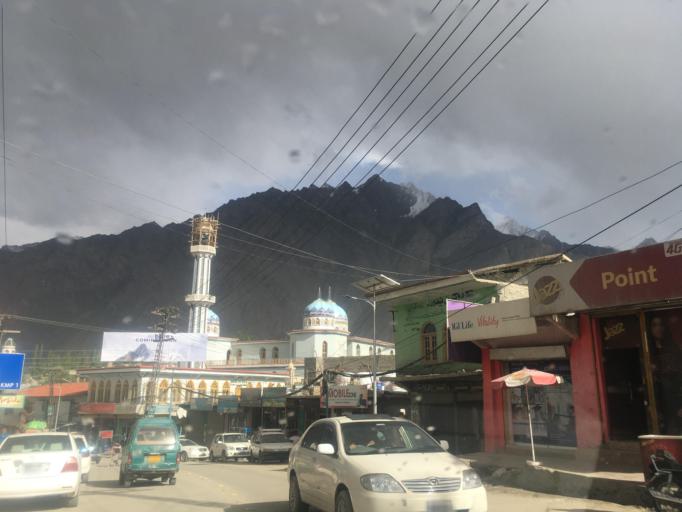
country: PK
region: Gilgit-Baltistan
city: Skardu
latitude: 35.2979
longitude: 75.6370
